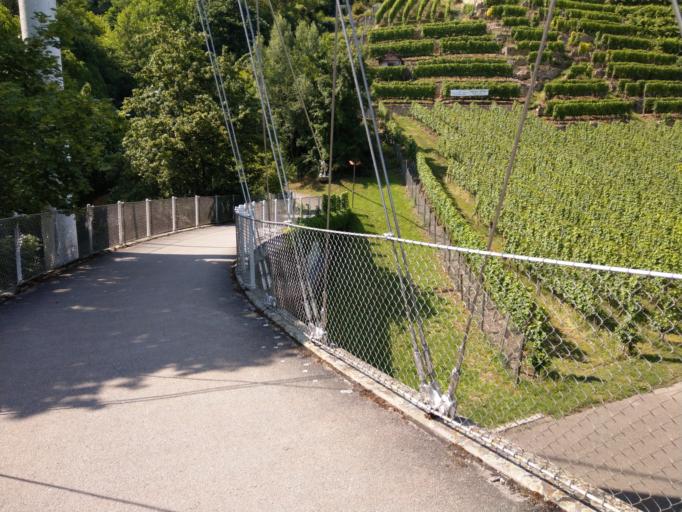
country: DE
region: Baden-Wuerttemberg
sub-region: Regierungsbezirk Stuttgart
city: Stuttgart Muehlhausen
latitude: 48.8344
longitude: 9.2084
